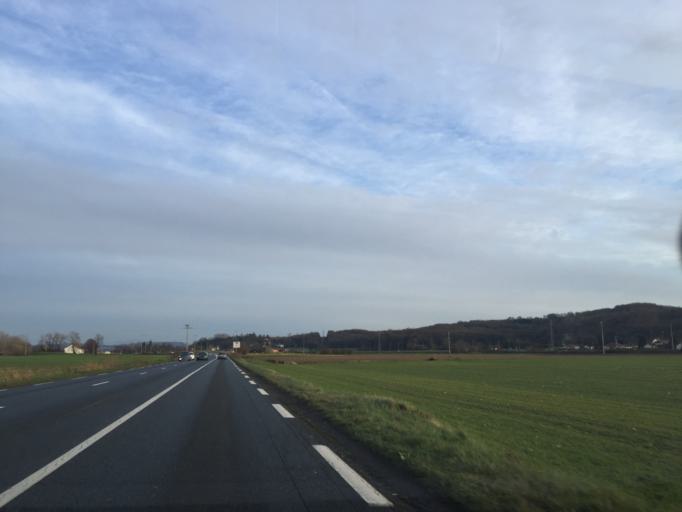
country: FR
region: Rhone-Alpes
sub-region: Departement de l'Isere
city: Vaulx-Milieu
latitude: 45.6155
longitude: 5.1924
